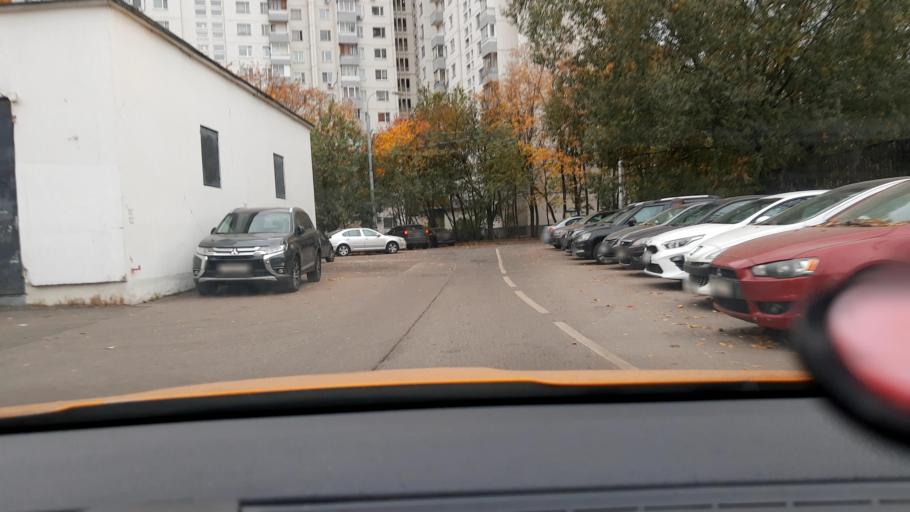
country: RU
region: Moskovskaya
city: Bol'shaya Setun'
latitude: 55.7238
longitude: 37.4418
